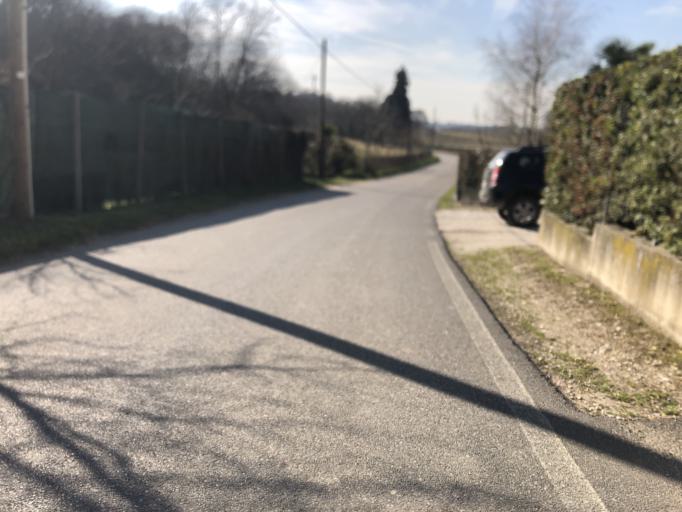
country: IT
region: Veneto
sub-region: Provincia di Verona
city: San Giorgio in Salici
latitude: 45.3989
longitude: 10.7732
